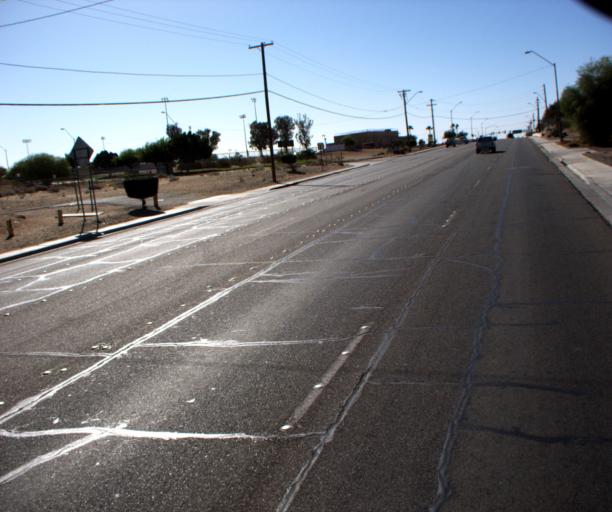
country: US
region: Arizona
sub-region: Yuma County
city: San Luis
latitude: 32.4976
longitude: -114.7854
